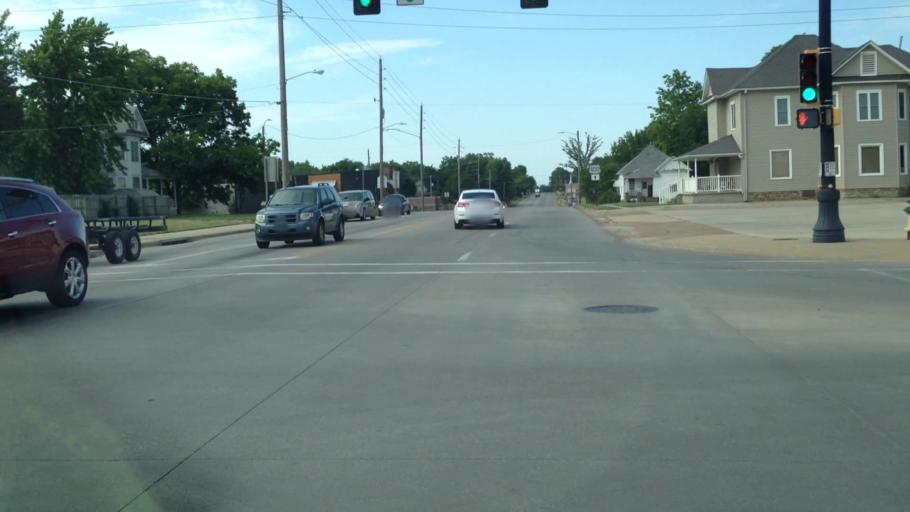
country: US
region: Kansas
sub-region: Labette County
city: Parsons
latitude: 37.3405
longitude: -95.2592
